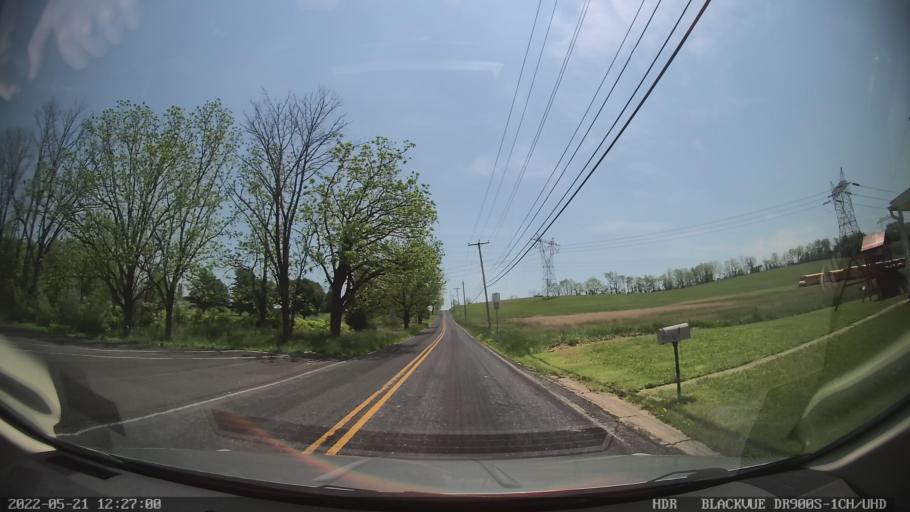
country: US
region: Pennsylvania
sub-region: Berks County
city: Bally
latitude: 40.3771
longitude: -75.6090
